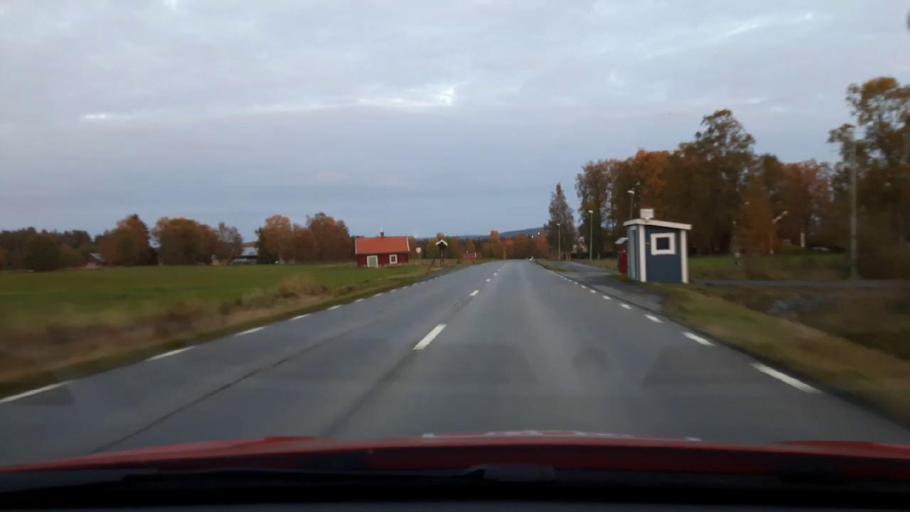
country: SE
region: Jaemtland
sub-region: OEstersunds Kommun
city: Ostersund
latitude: 63.2258
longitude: 14.5949
